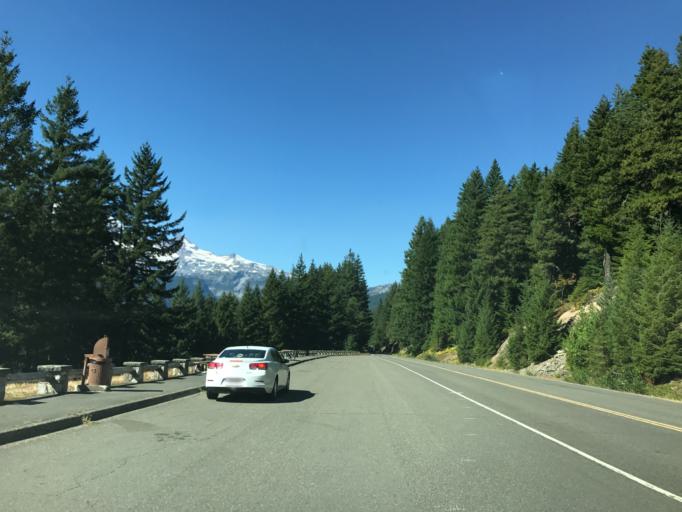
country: US
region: Washington
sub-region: Pierce County
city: Buckley
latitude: 46.7102
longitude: -121.6005
